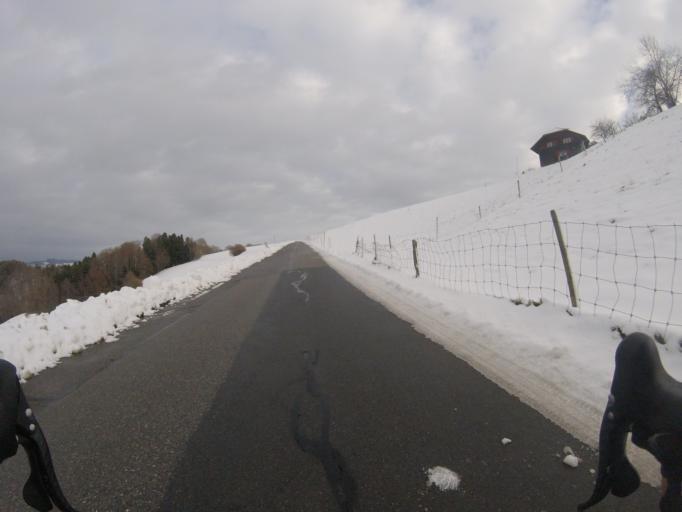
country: CH
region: Bern
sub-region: Bern-Mittelland District
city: Kehrsatz
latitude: 46.8959
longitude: 7.4459
